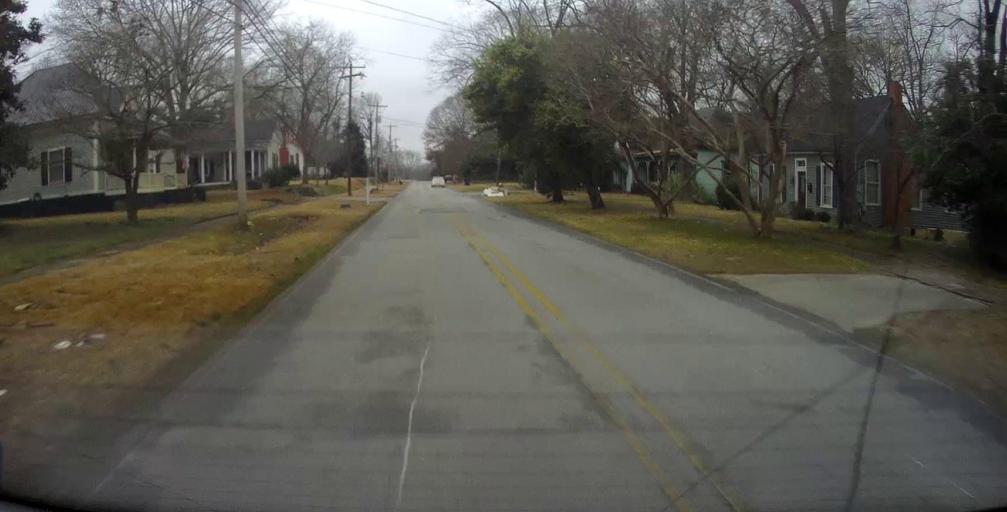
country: US
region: Georgia
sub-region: Lamar County
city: Barnesville
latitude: 33.0546
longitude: -84.1611
